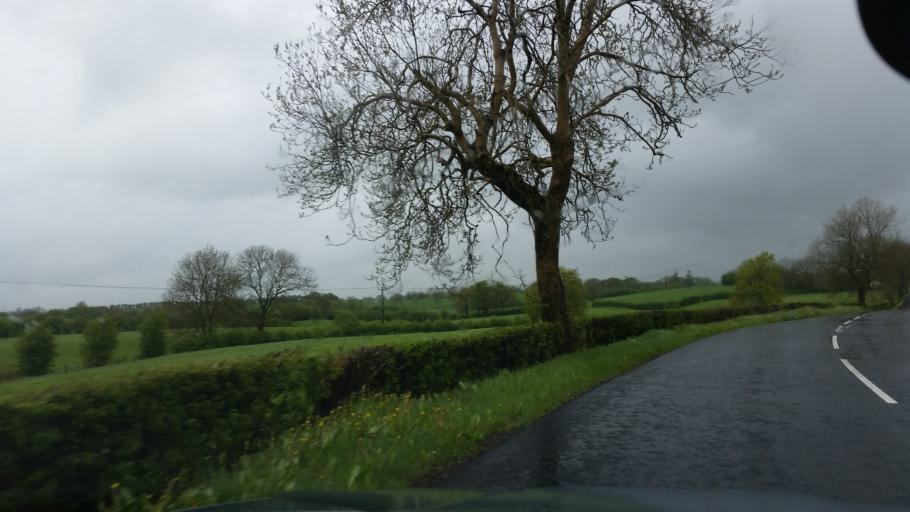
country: GB
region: Northern Ireland
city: Fintona
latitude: 54.5230
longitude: -7.2965
